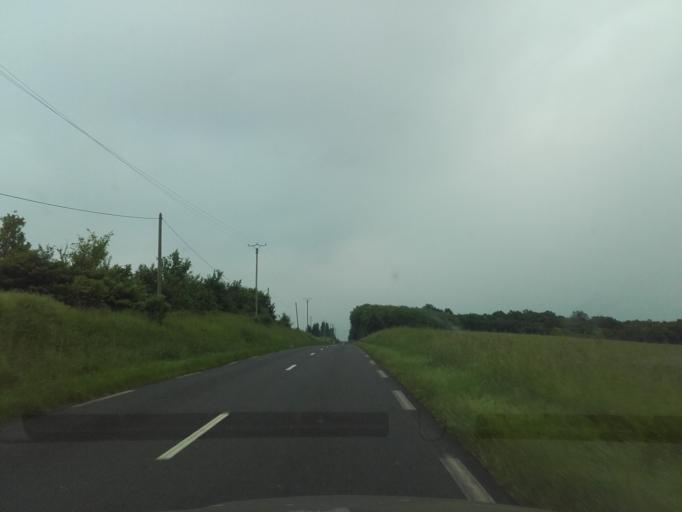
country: FR
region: Centre
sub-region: Departement d'Indre-et-Loire
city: Beaumont-la-Ronce
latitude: 47.5526
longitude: 0.6856
